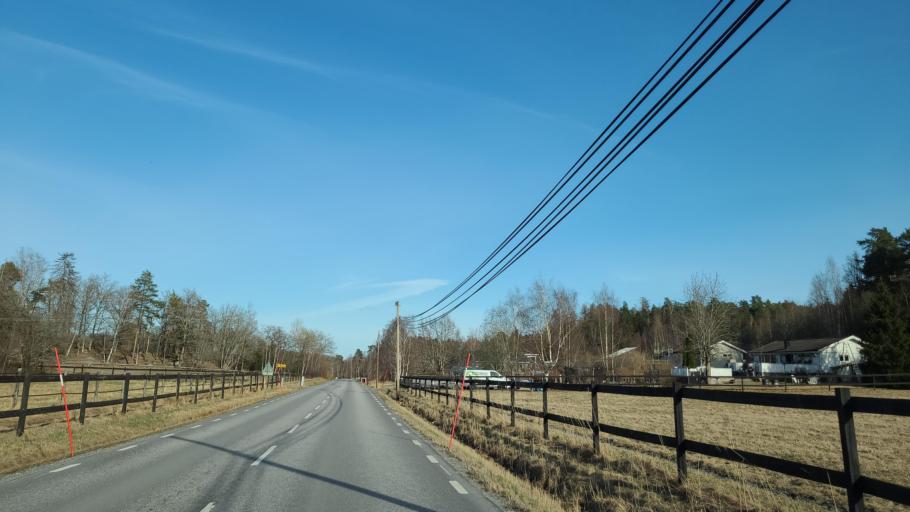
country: SE
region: Stockholm
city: Stenhamra
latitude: 59.2765
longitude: 17.6962
